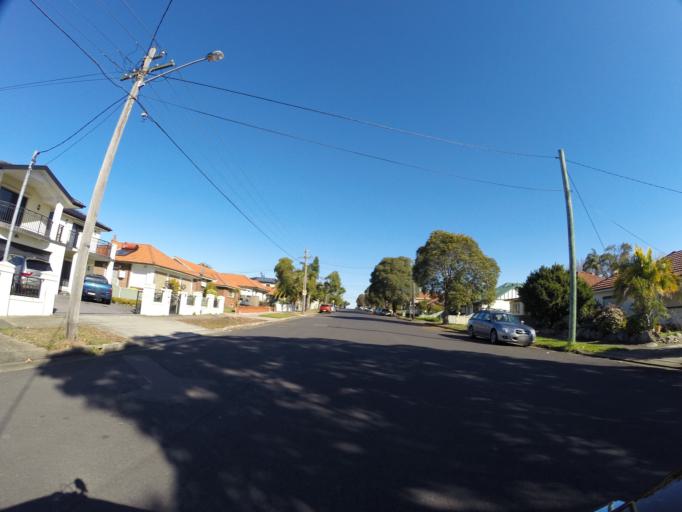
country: AU
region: New South Wales
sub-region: Auburn
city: Lidcombe
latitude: -33.8549
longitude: 151.0571
